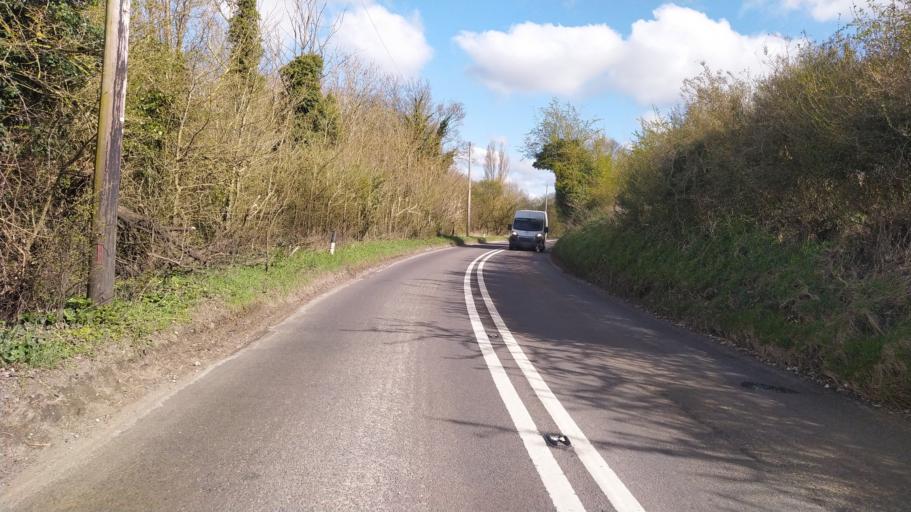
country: GB
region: England
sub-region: Wiltshire
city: Collingbourne Kingston
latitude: 51.2784
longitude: -1.6525
